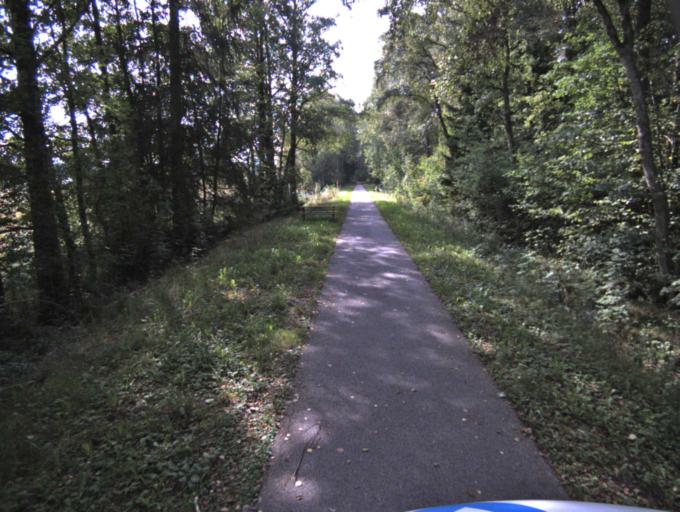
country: SE
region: Vaestra Goetaland
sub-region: Tranemo Kommun
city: Limmared
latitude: 57.6262
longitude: 13.3478
